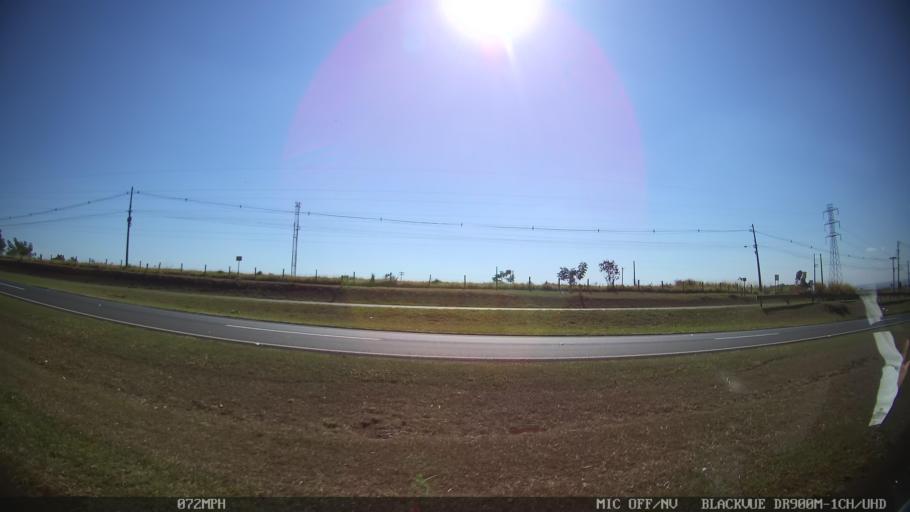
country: BR
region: Sao Paulo
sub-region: Ribeirao Preto
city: Ribeirao Preto
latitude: -21.1298
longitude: -47.8494
